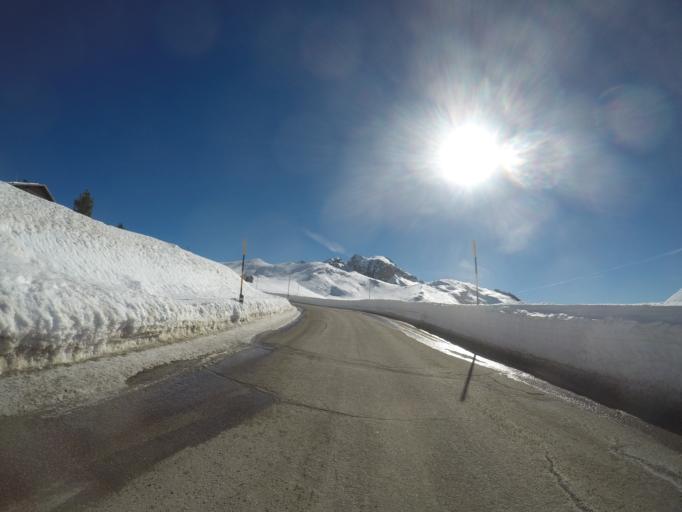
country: IT
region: Veneto
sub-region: Provincia di Belluno
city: Selva di Cadore
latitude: 46.4850
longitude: 12.0456
